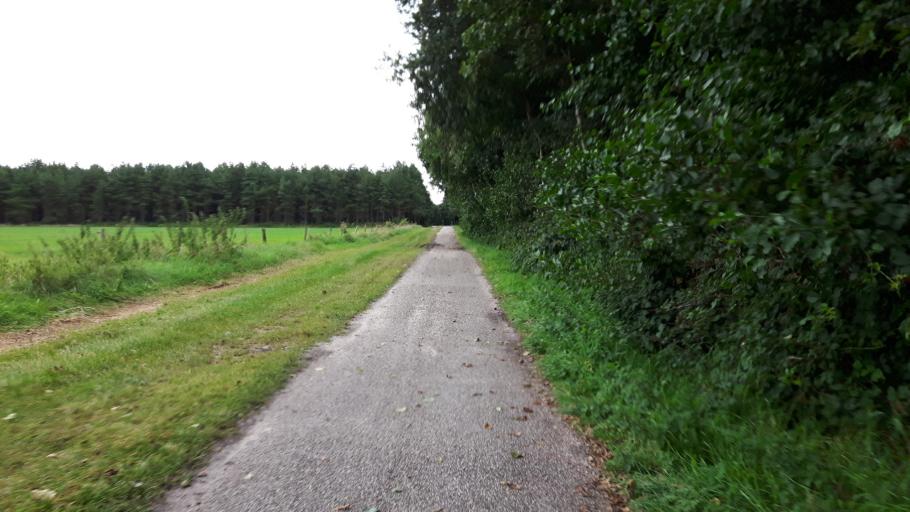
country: NL
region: Friesland
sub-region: Gemeente Ameland
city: Nes
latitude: 53.4488
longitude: 5.7129
